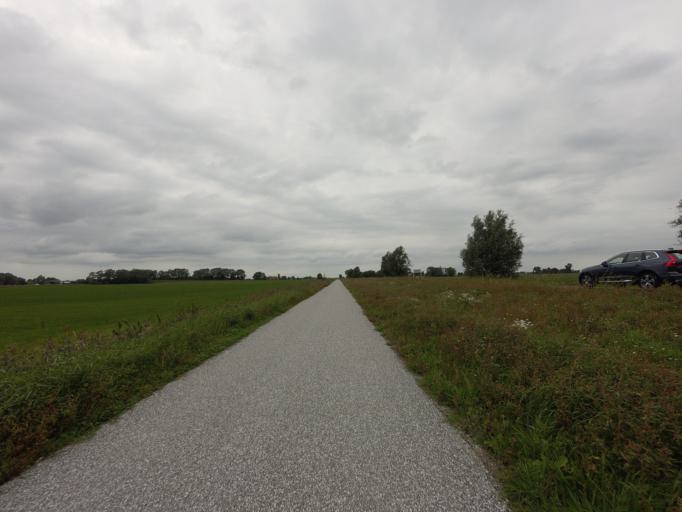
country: NL
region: Friesland
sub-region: Sudwest Fryslan
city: IJlst
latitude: 53.0421
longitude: 5.6213
